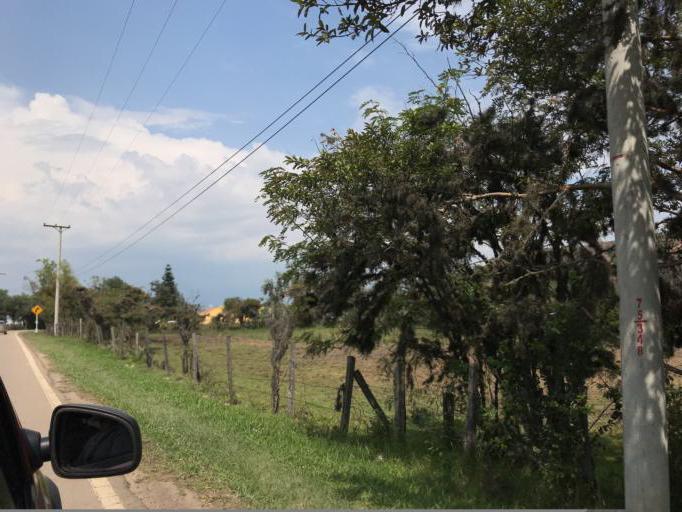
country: CO
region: Boyaca
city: Sutamarchan
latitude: 5.6105
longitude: -73.6297
